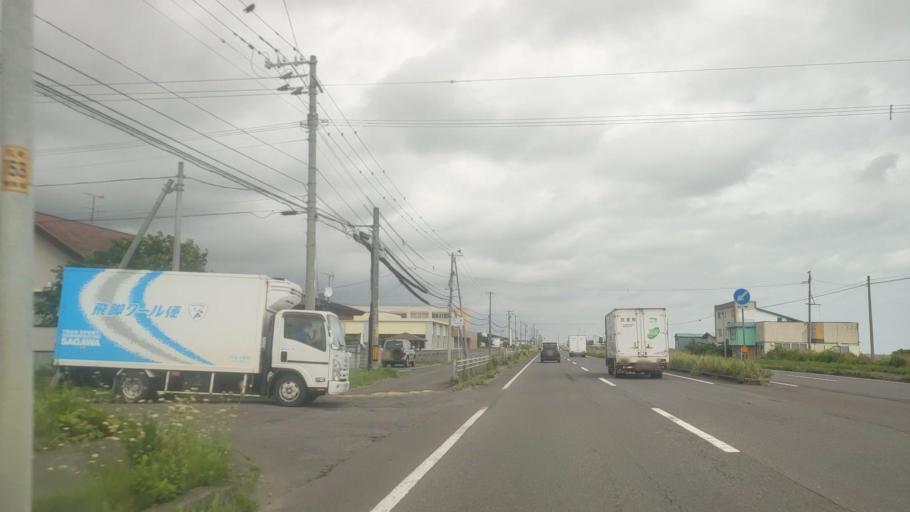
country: JP
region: Hokkaido
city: Shiraoi
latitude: 42.4701
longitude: 141.2298
